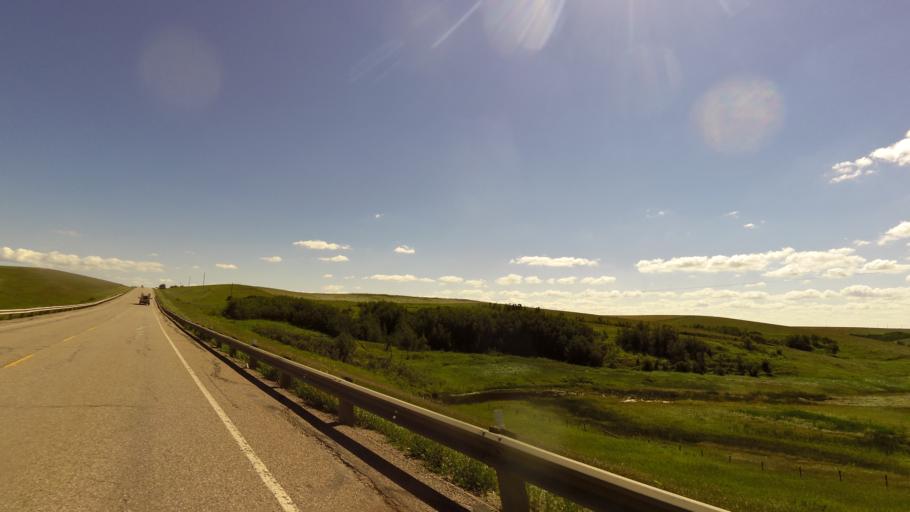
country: CA
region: Saskatchewan
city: Lloydminster
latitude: 52.8419
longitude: -110.0322
